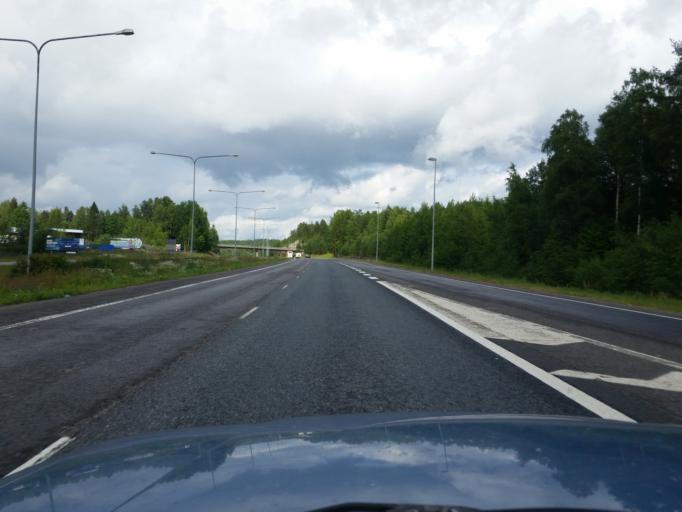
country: FI
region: Paijanne Tavastia
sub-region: Lahti
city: Heinola
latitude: 61.2373
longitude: 26.0460
